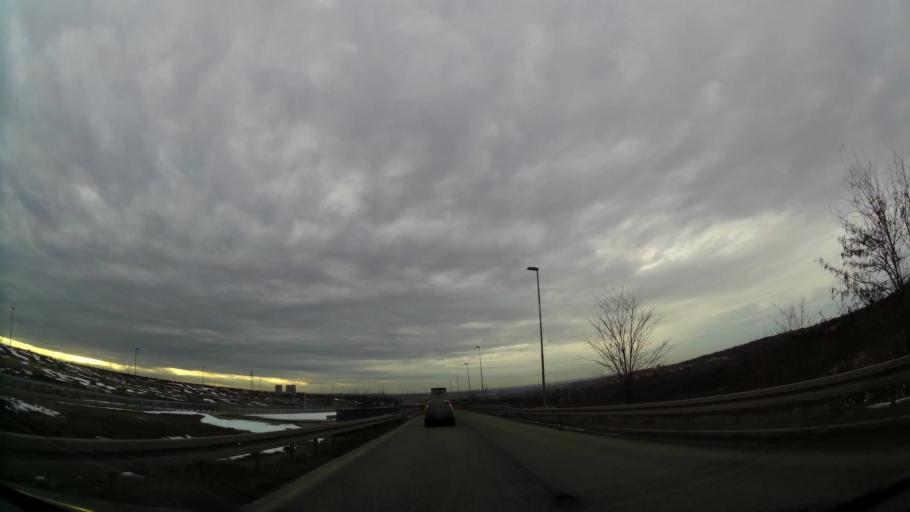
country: RS
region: Central Serbia
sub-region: Belgrade
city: Rakovica
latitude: 44.7144
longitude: 20.4113
